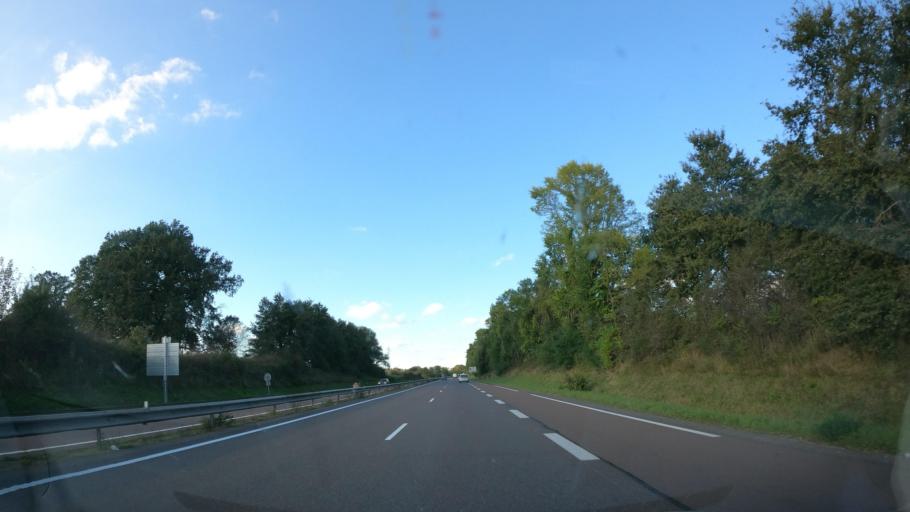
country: FR
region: Bourgogne
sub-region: Departement de Saone-et-Loire
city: Saint-Vallier
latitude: 46.6464
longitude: 4.3297
